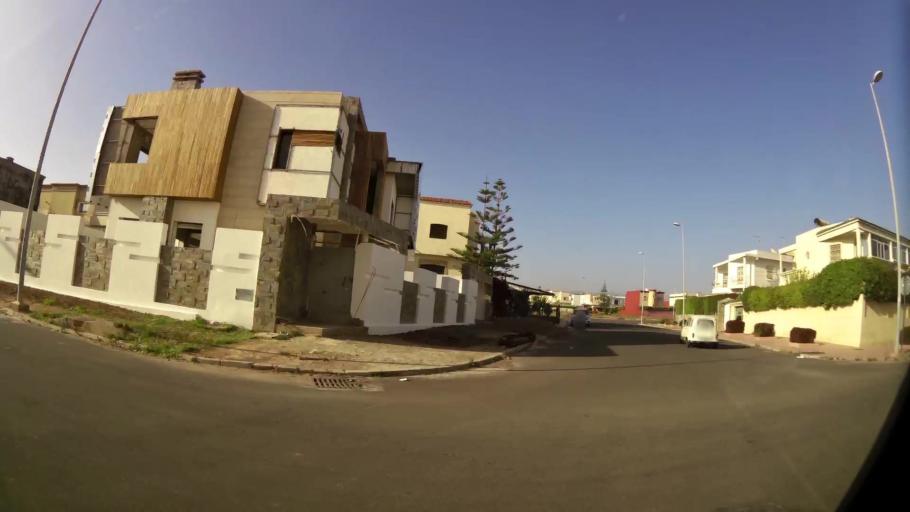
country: MA
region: Oued ed Dahab-Lagouira
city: Dakhla
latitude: 30.4009
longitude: -9.5394
